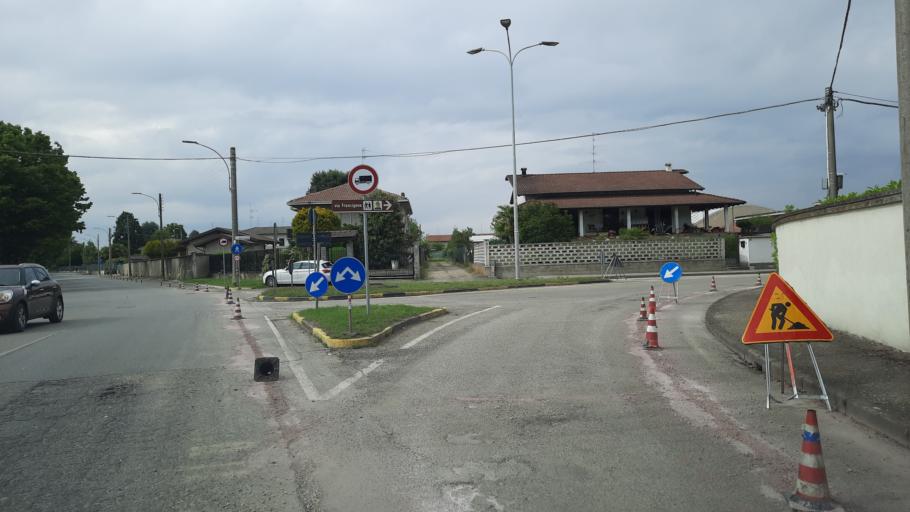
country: IT
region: Lombardy
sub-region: Provincia di Pavia
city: Robbio
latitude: 45.2866
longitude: 8.5862
